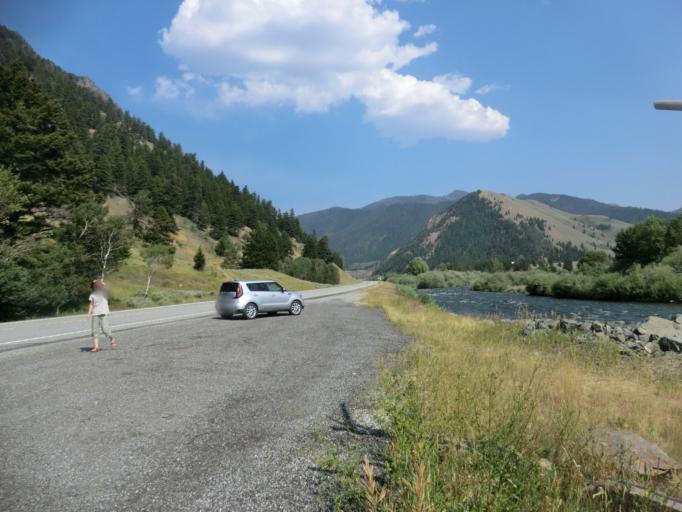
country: US
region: Montana
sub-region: Gallatin County
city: West Yellowstone
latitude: 44.8266
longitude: -111.4562
